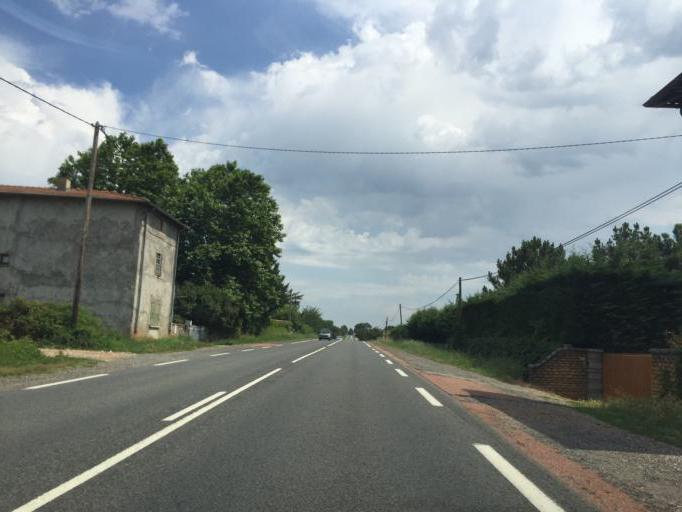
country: FR
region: Rhone-Alpes
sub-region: Departement du Rhone
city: Bully
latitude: 45.8607
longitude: 4.5598
